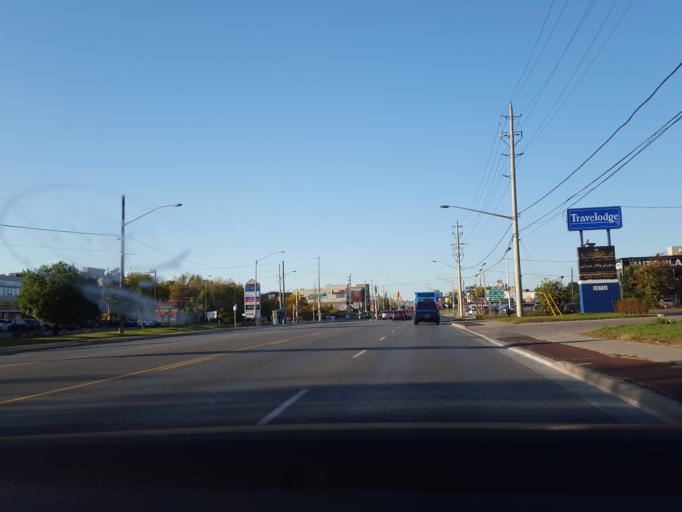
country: CA
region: Ontario
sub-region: York
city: Richmond Hill
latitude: 43.8883
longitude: -79.4411
